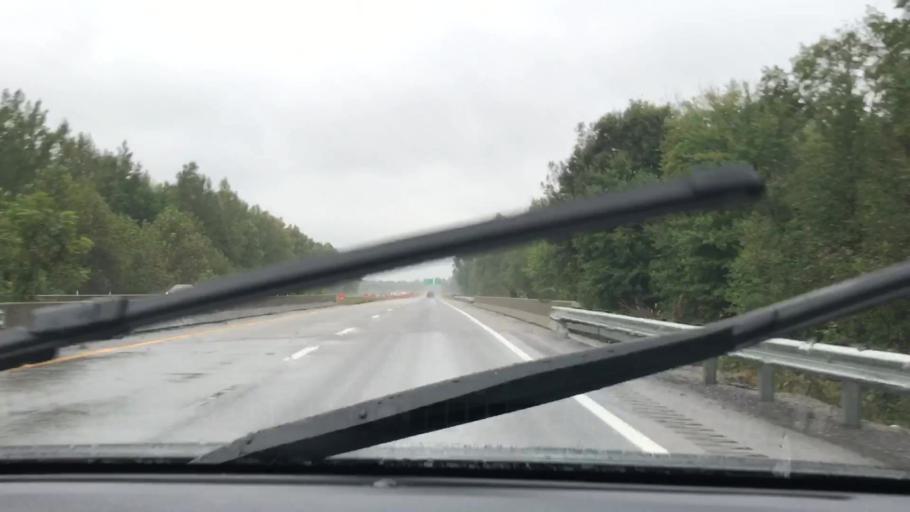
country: US
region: Kentucky
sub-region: Hopkins County
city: Nortonville
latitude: 37.1589
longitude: -87.4593
